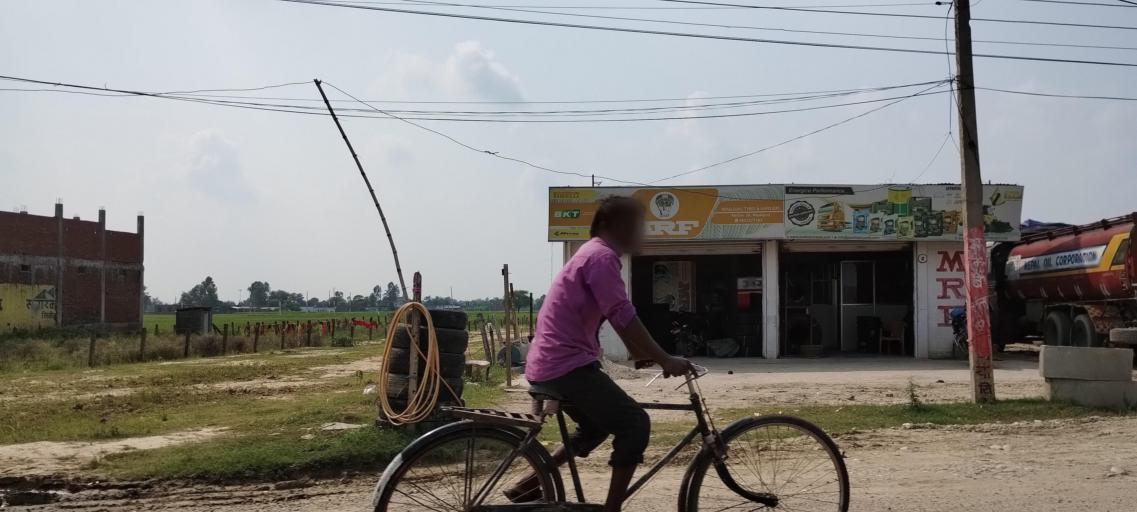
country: NP
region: Mid Western
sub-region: Bheri Zone
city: Nepalgunj
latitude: 28.1045
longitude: 81.6549
